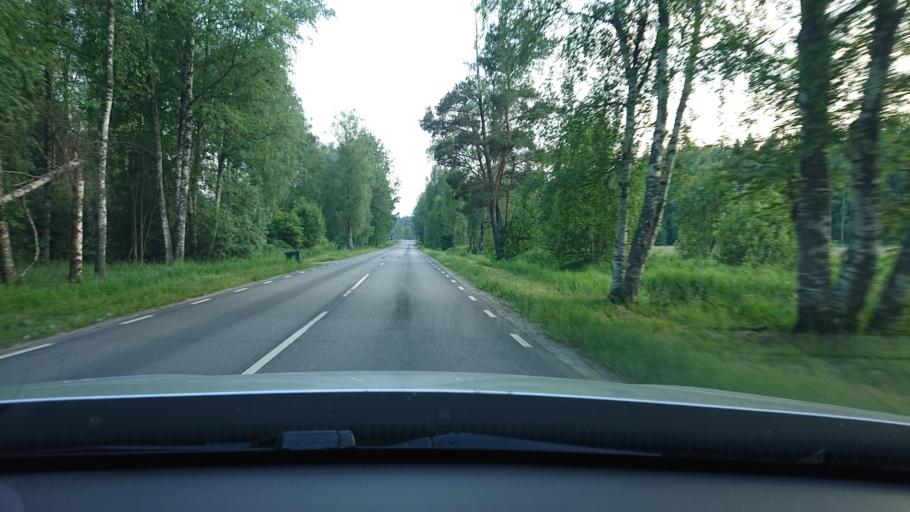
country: SE
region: Stockholm
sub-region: Vaxholms Kommun
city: Resaro
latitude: 59.4723
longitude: 18.3748
